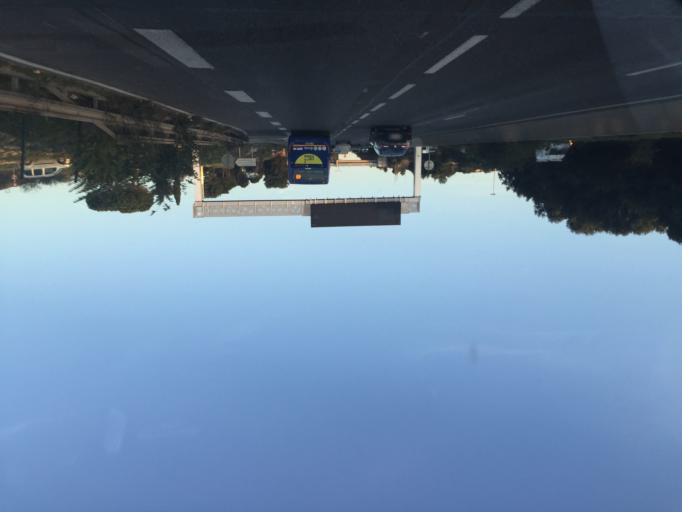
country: FR
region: Provence-Alpes-Cote d'Azur
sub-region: Departement des Bouches-du-Rhone
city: Marseille 15
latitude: 43.3882
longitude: 5.3511
